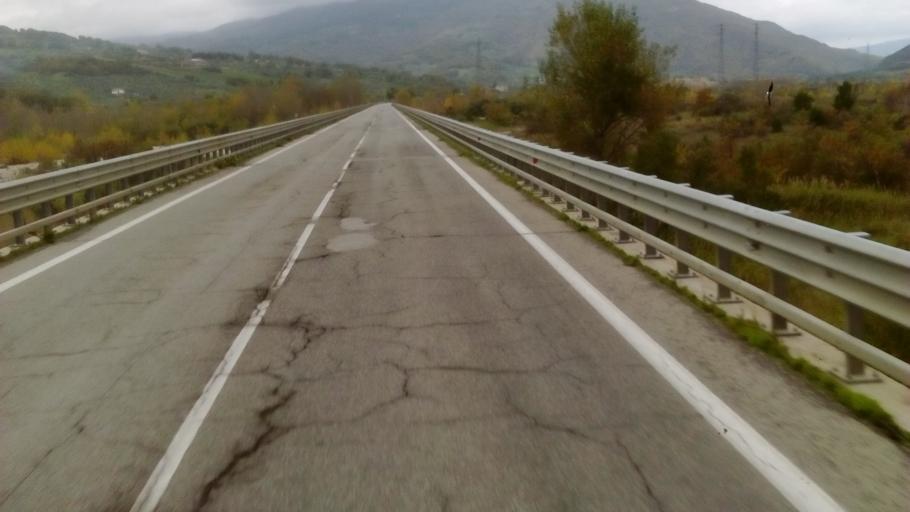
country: IT
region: Abruzzo
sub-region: Provincia di Chieti
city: Celenza sul Trigno
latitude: 41.8722
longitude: 14.6038
